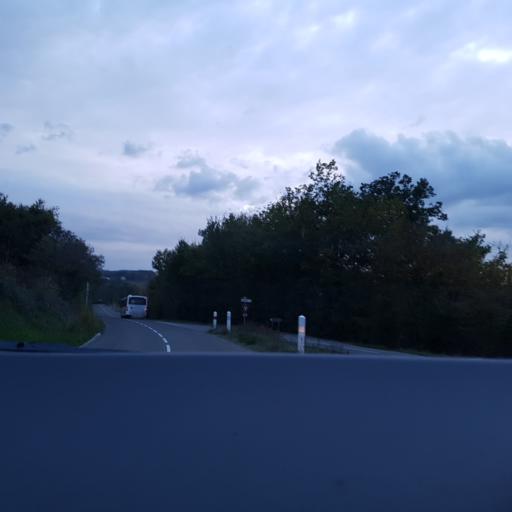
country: FR
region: Midi-Pyrenees
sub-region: Departement du Gers
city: Condom
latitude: 43.9510
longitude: 0.3047
